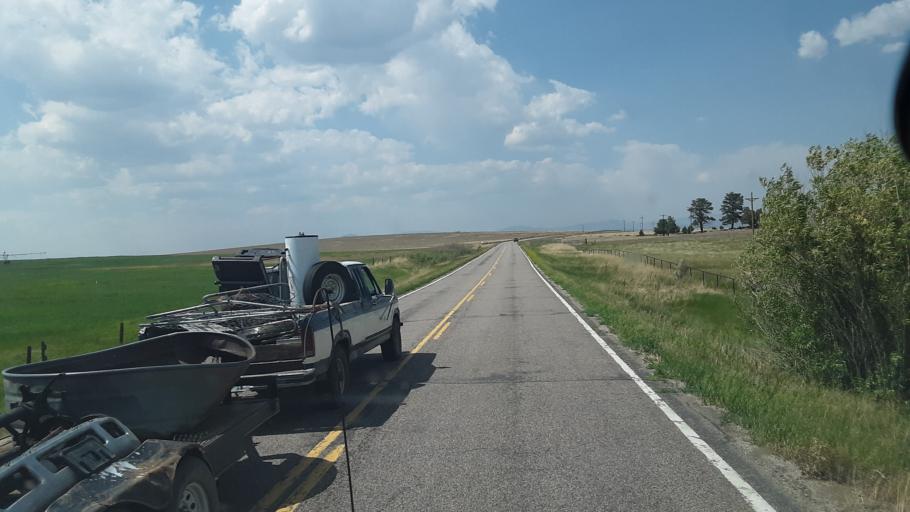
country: US
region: Colorado
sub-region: Custer County
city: Westcliffe
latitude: 38.2734
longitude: -105.6149
